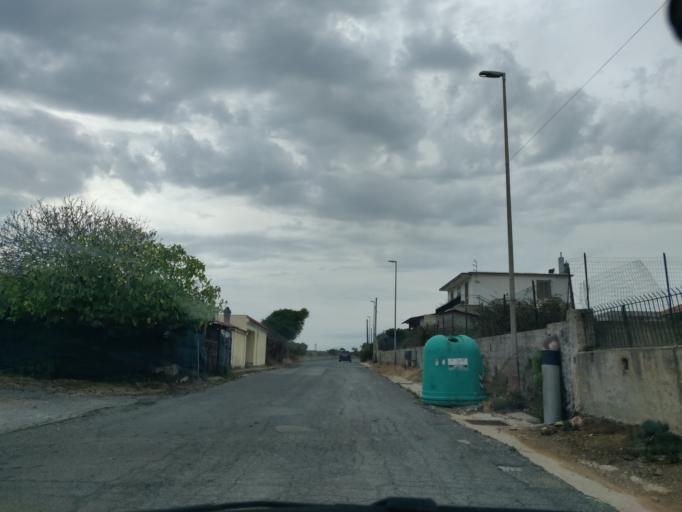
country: IT
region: Latium
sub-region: Citta metropolitana di Roma Capitale
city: Santa Marinella
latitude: 42.0410
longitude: 11.9114
